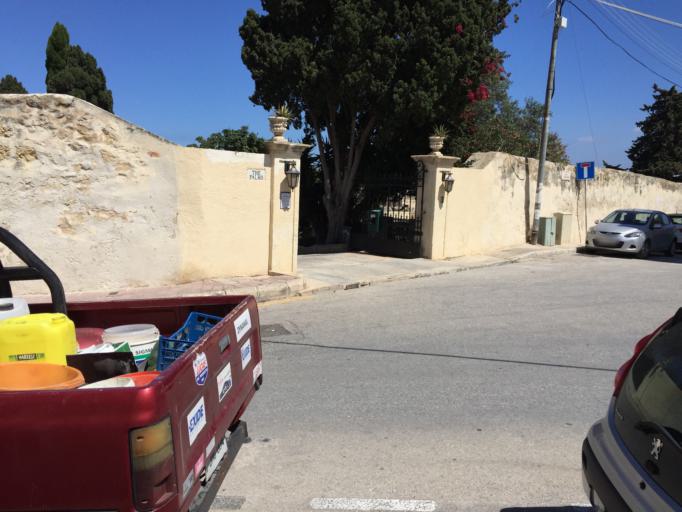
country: MT
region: Saint Julian
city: San Giljan
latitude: 35.9141
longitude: 14.4902
